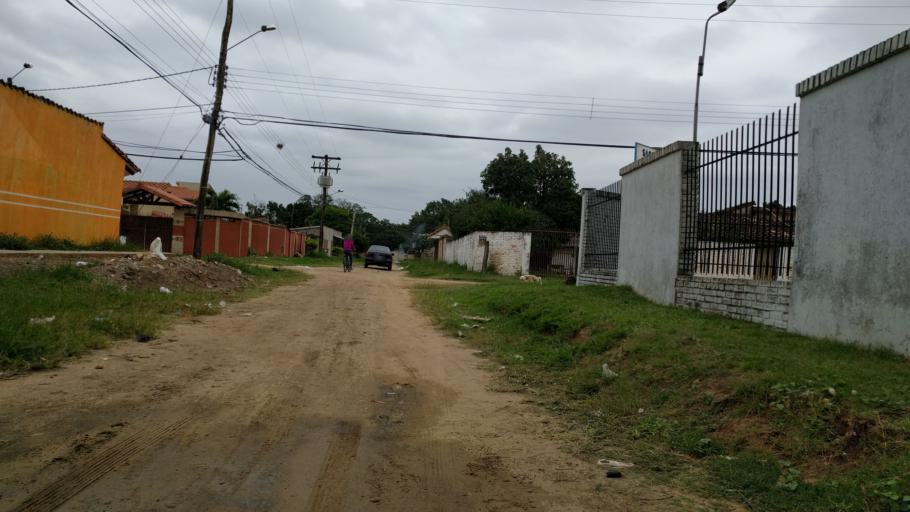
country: BO
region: Santa Cruz
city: Santa Cruz de la Sierra
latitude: -17.8065
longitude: -63.2174
